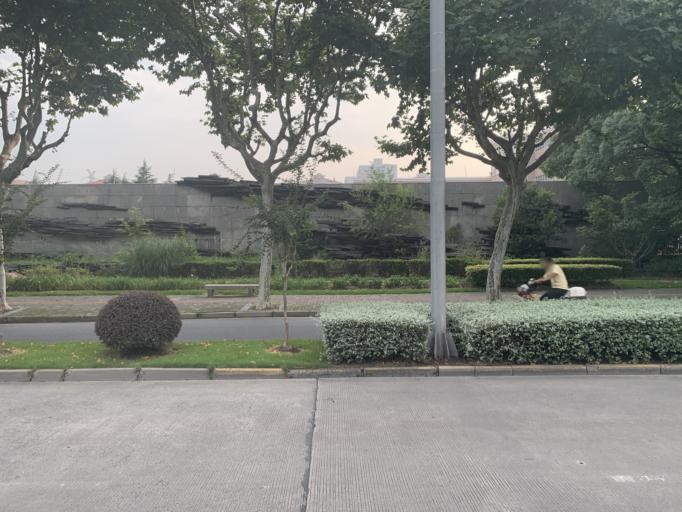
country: CN
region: Shanghai Shi
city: Huamu
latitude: 31.2456
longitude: 121.5719
